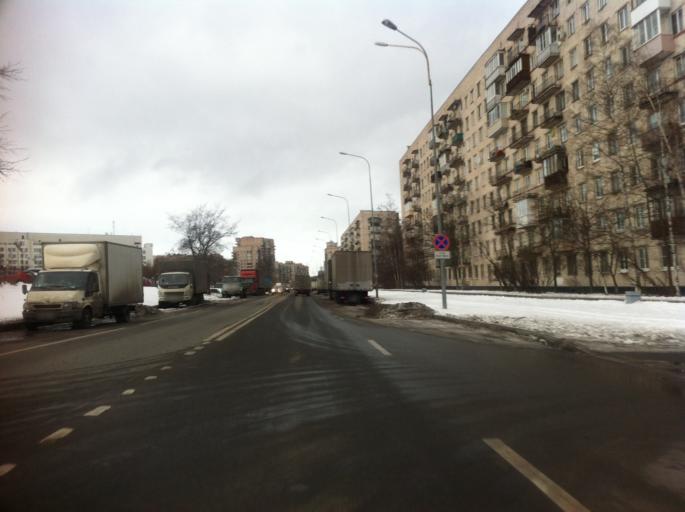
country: RU
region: St.-Petersburg
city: Dachnoye
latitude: 59.8364
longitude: 30.2447
